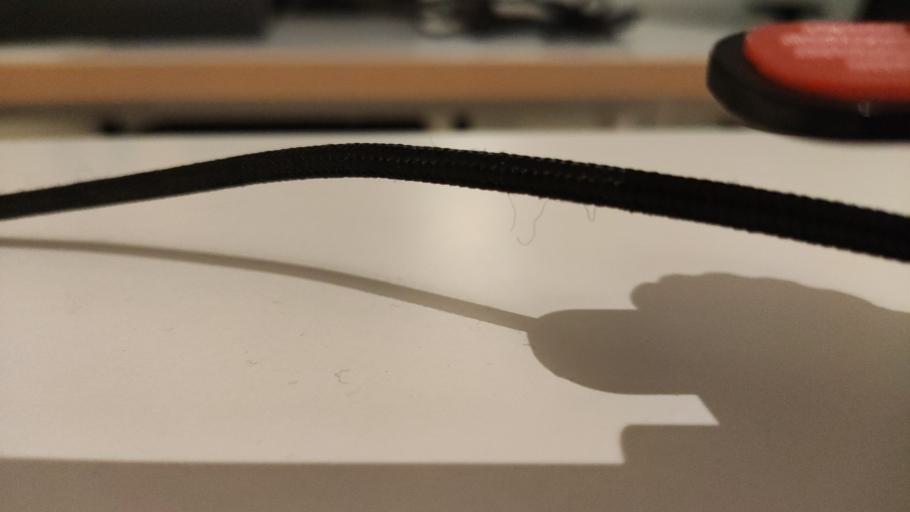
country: RU
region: Moskovskaya
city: Novoye
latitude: 55.6349
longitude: 38.9293
